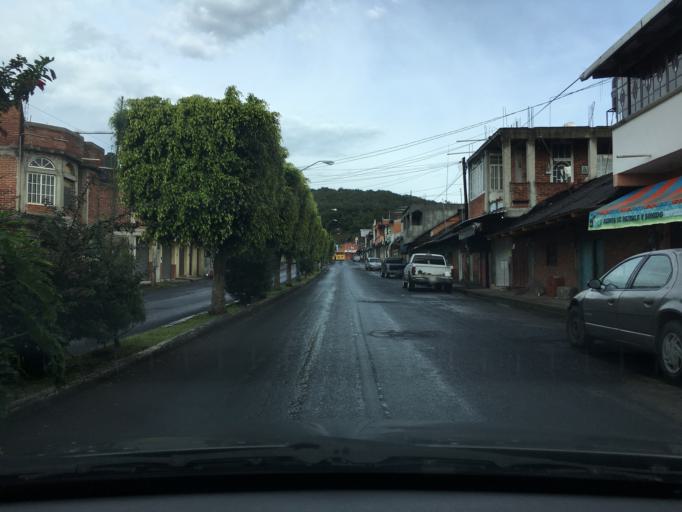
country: MX
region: Michoacan
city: Nuevo San Juan Parangaricutiro
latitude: 19.4188
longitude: -102.1316
